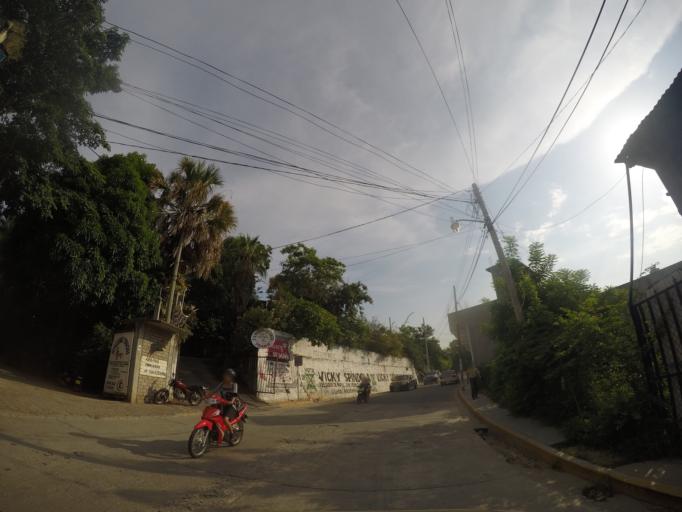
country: MX
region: Oaxaca
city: San Pedro Pochutla
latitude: 15.7484
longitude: -96.4670
